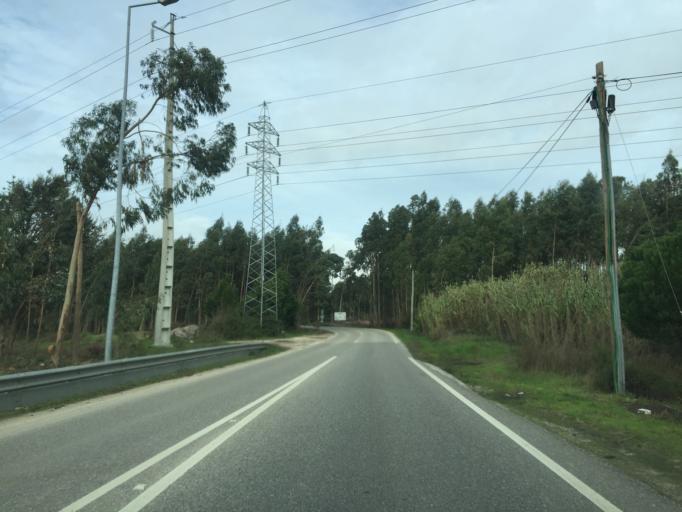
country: PT
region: Coimbra
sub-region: Figueira da Foz
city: Lavos
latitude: 40.0502
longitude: -8.8156
